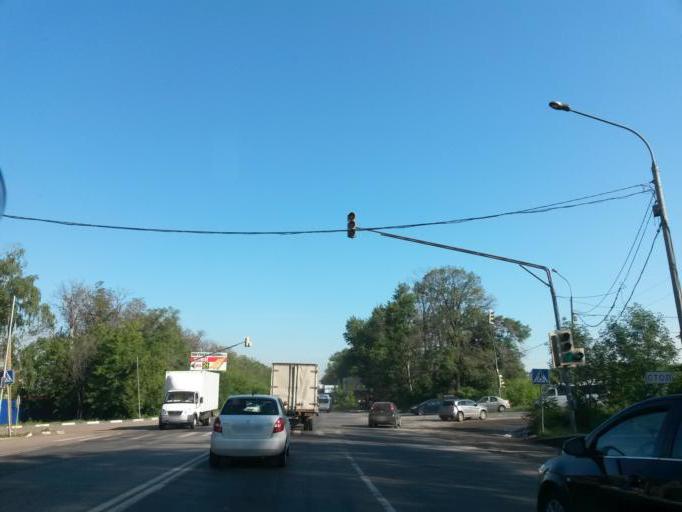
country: RU
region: Moskovskaya
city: Petrovskaya
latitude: 55.5606
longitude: 37.7721
